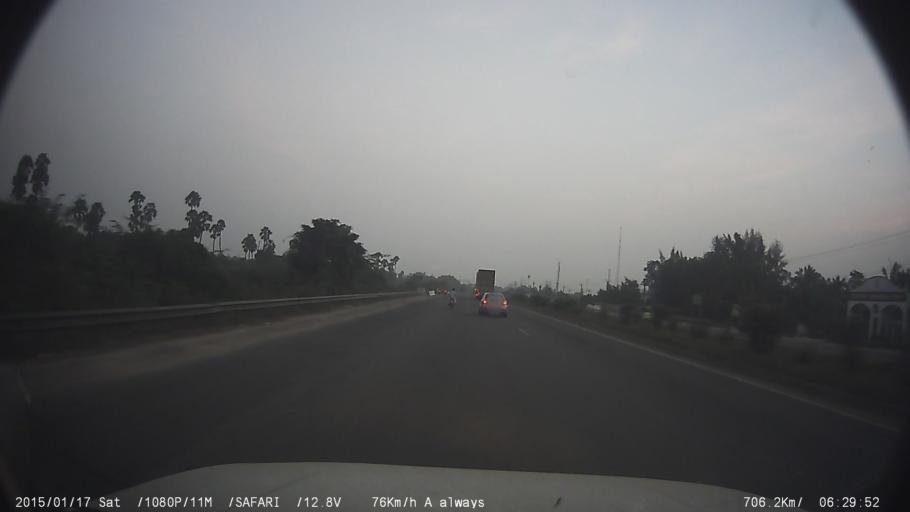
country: IN
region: Tamil Nadu
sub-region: Kancheepuram
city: Sriperumbudur
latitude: 12.9456
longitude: 79.9231
